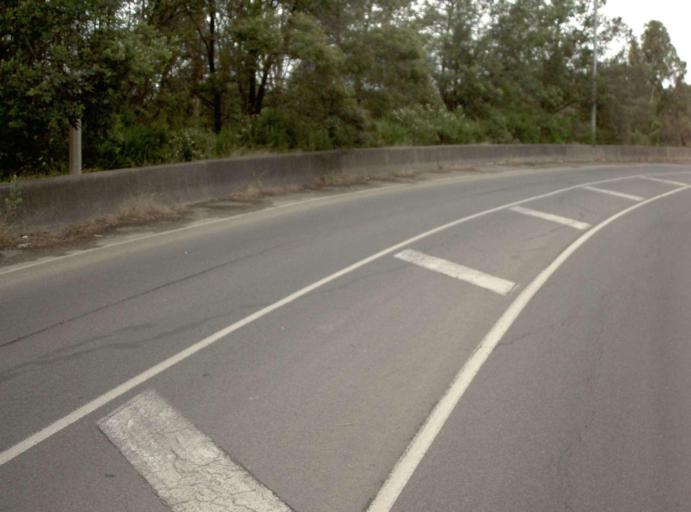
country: AU
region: Victoria
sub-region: Baw Baw
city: Warragul
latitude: -38.1714
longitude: 145.9705
